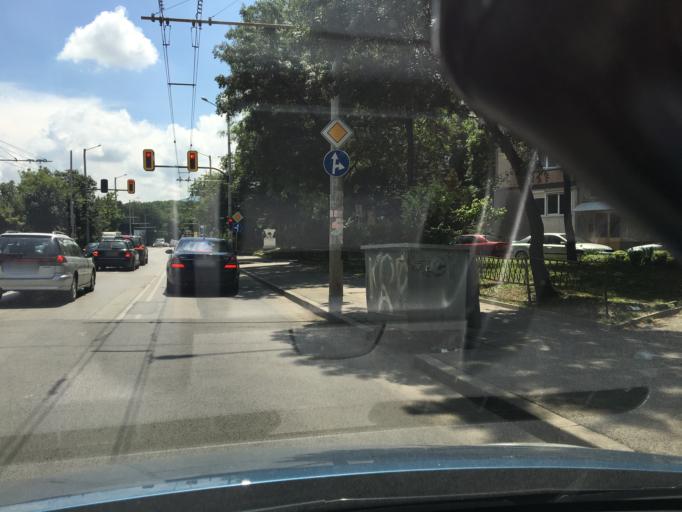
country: BG
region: Sofia-Capital
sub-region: Stolichna Obshtina
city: Sofia
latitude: 42.6753
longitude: 23.3035
